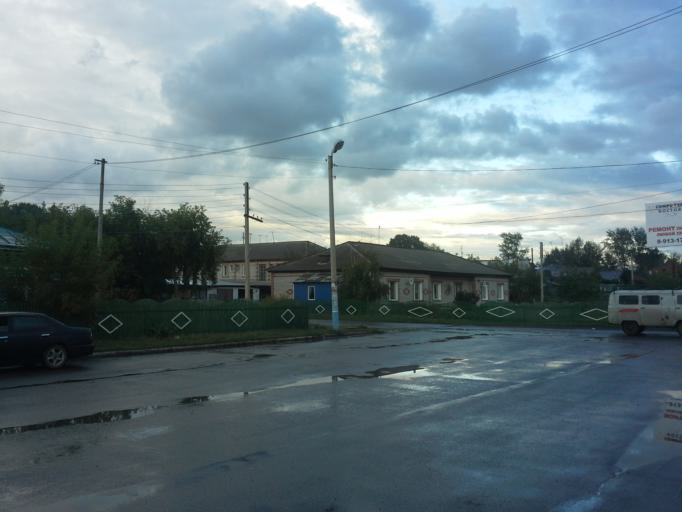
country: RU
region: Krasnoyarskiy
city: Ilanskiy
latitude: 56.2394
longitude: 96.0715
